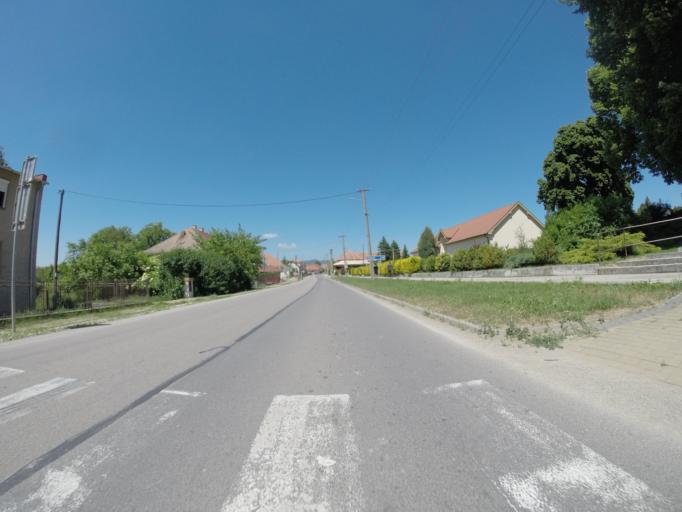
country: SK
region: Trnavsky
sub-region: Okres Trnava
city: Piestany
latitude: 48.5002
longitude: 17.9834
